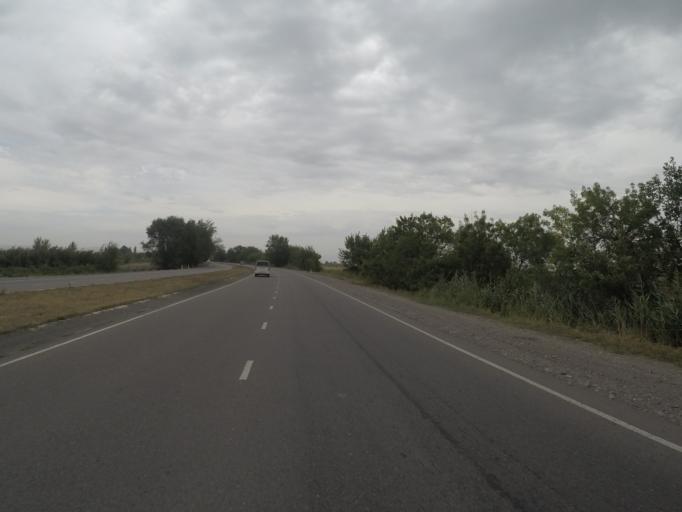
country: KG
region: Chuy
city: Lebedinovka
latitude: 42.9246
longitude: 74.7620
